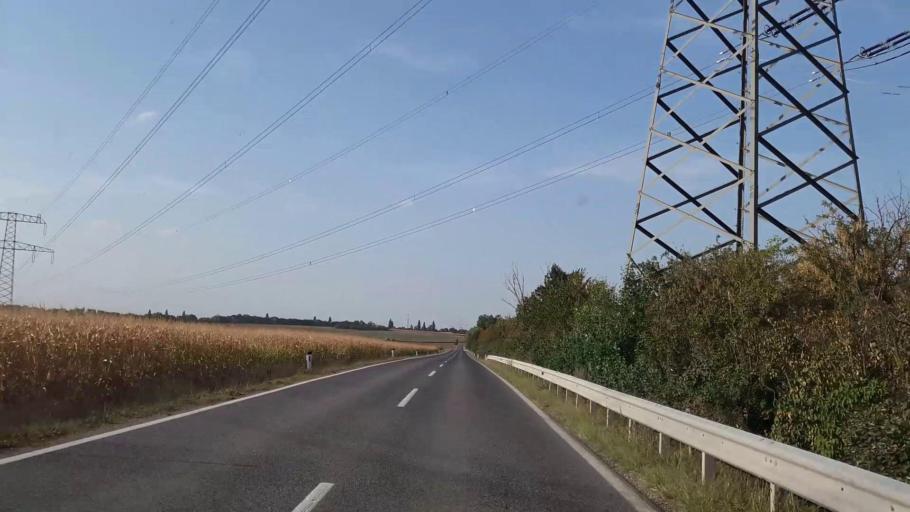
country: AT
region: Lower Austria
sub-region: Politischer Bezirk Ganserndorf
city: Mannsdorf an der Donau
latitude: 48.0969
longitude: 16.6684
